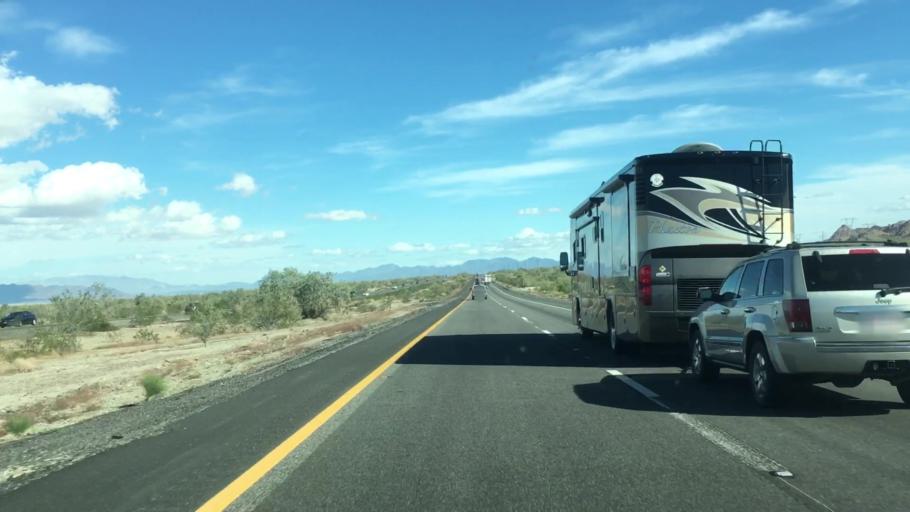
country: US
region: California
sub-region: Imperial County
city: Niland
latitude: 33.6917
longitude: -115.5002
